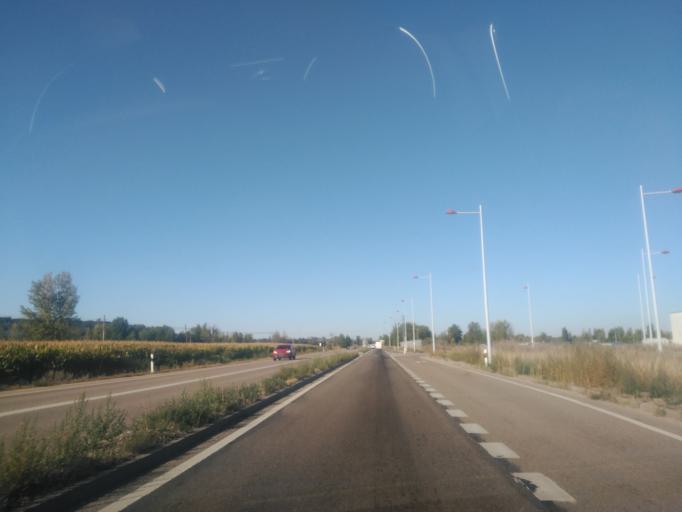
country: ES
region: Castille and Leon
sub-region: Provincia de Burgos
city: Villalba de Duero
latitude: 41.6638
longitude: -3.7343
